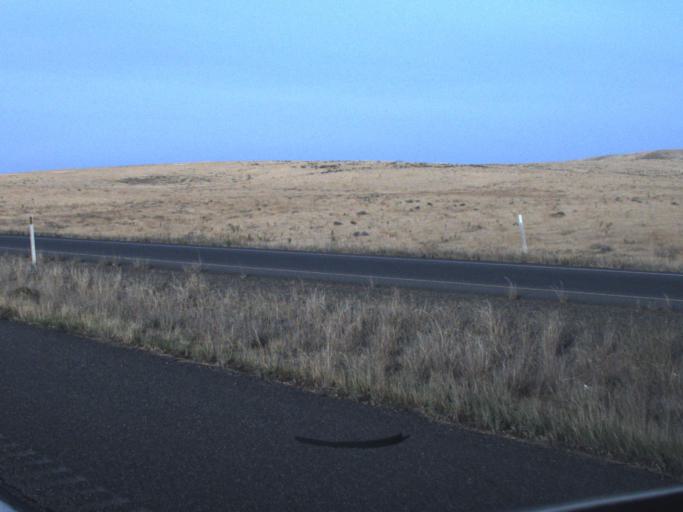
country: US
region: Oregon
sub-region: Umatilla County
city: Umatilla
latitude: 45.9635
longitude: -119.3423
